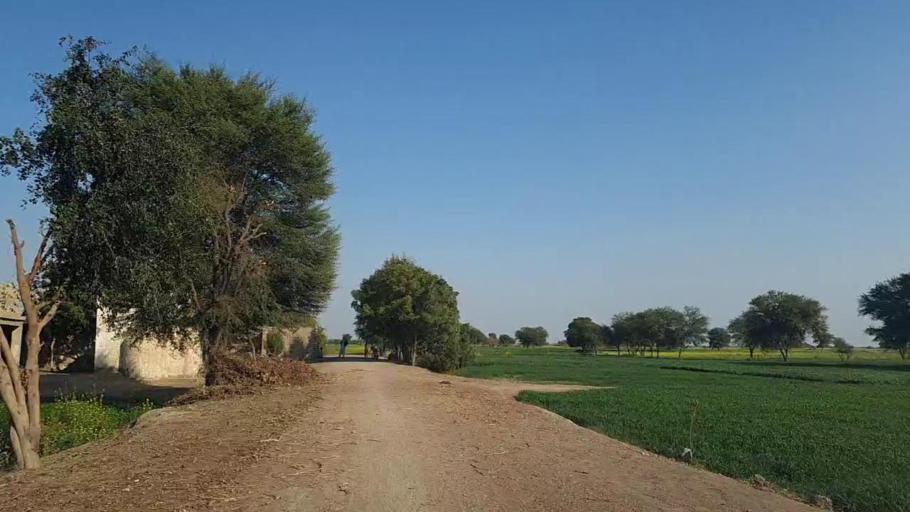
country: PK
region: Sindh
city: Shahpur Chakar
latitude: 26.2012
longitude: 68.6539
